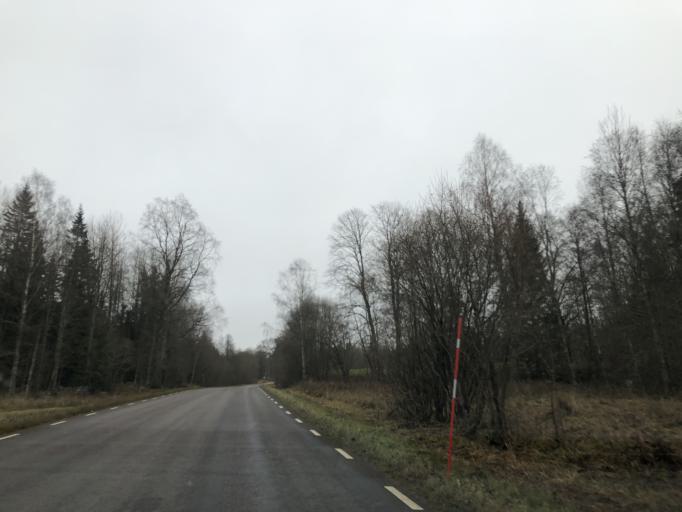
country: SE
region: Vaestra Goetaland
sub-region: Ulricehamns Kommun
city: Ulricehamn
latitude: 57.7680
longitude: 13.4625
